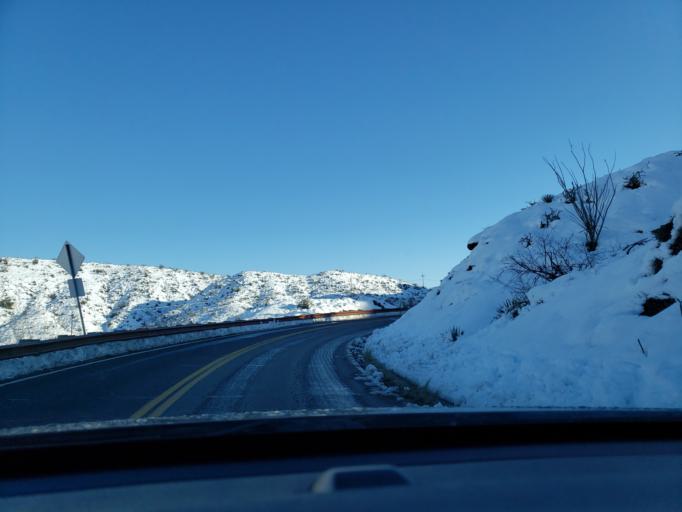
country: US
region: Arizona
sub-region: Maricopa County
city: Carefree
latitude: 33.8903
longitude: -111.8198
